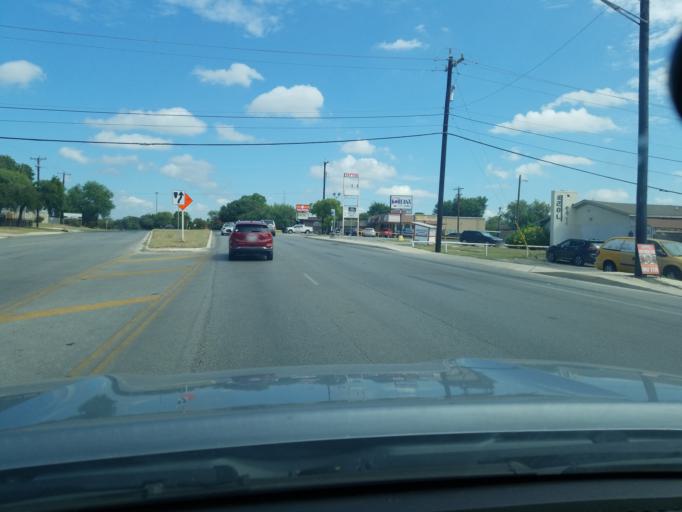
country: US
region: Texas
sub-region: Bexar County
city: Terrell Hills
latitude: 29.4863
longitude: -98.4300
